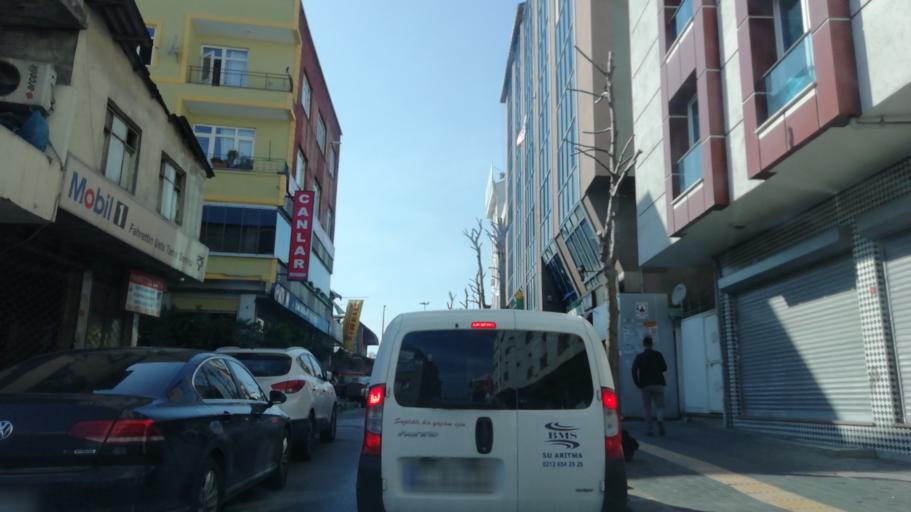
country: TR
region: Istanbul
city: Bahcelievler
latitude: 40.9944
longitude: 28.8363
